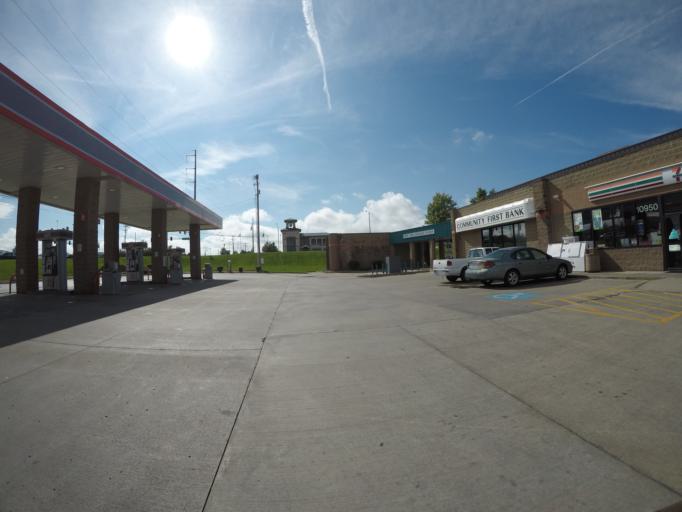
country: US
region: Kansas
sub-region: Wyandotte County
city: Edwardsville
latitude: 39.1291
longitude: -94.8343
